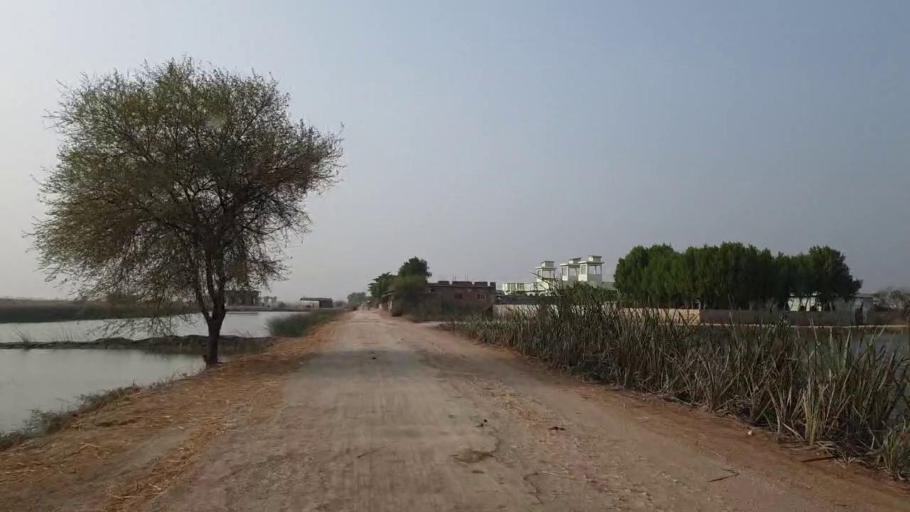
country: PK
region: Sindh
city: Matli
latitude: 25.0653
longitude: 68.6037
